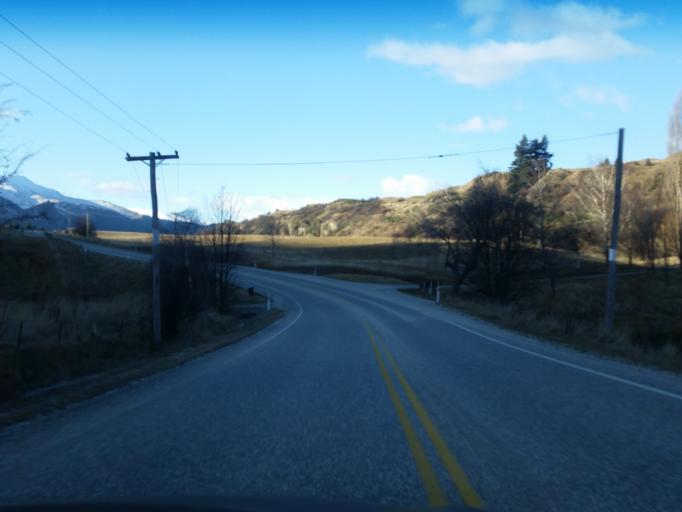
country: NZ
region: Otago
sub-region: Queenstown-Lakes District
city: Queenstown
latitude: -44.9706
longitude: 168.7013
